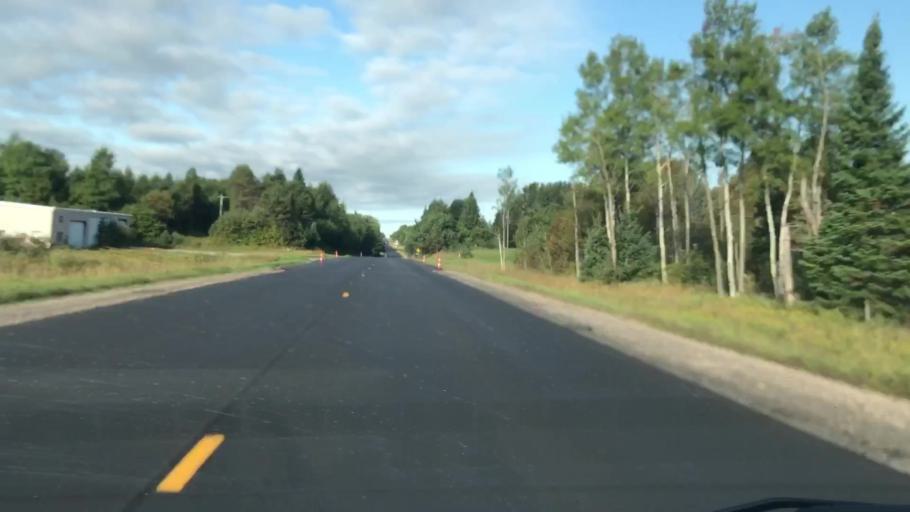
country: US
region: Michigan
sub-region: Mackinac County
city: Saint Ignace
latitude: 46.3460
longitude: -84.9526
